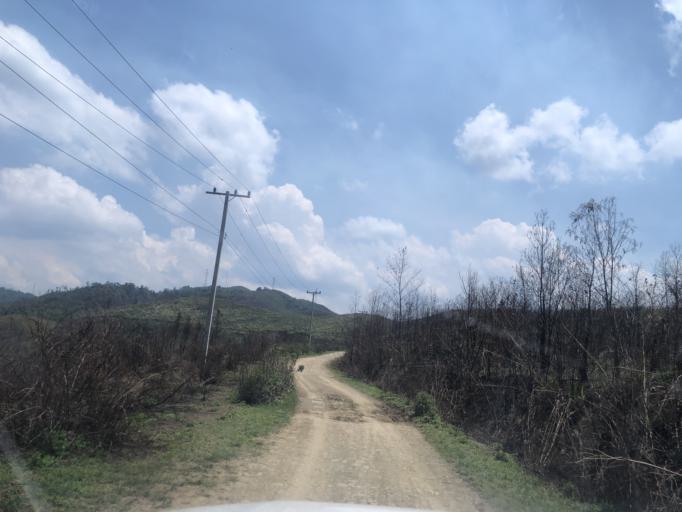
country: LA
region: Phongsali
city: Phongsali
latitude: 21.4078
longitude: 102.1864
